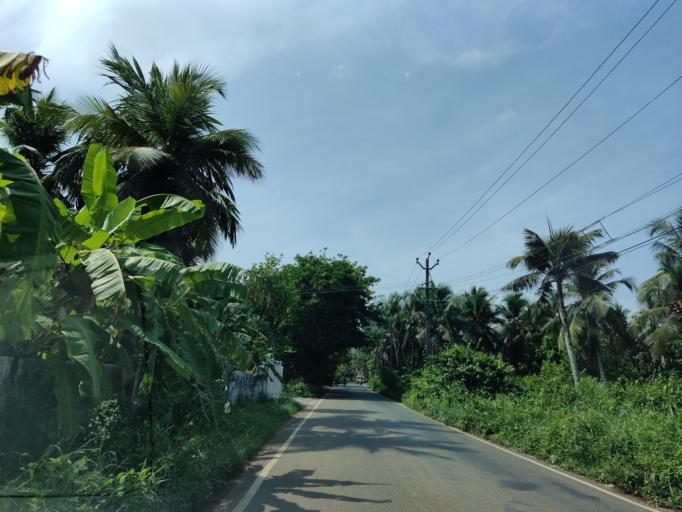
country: IN
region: Kerala
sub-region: Alappuzha
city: Mavelikara
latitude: 9.3303
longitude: 76.4673
